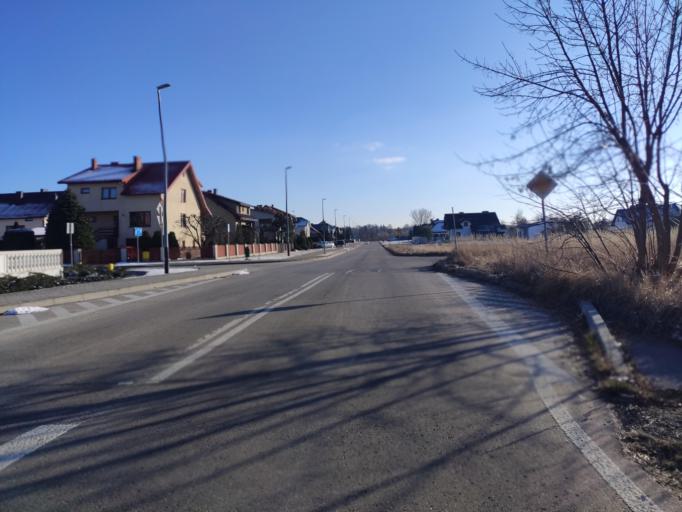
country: PL
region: Lublin Voivodeship
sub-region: Powiat lubartowski
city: Kock
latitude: 51.6422
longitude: 22.4301
